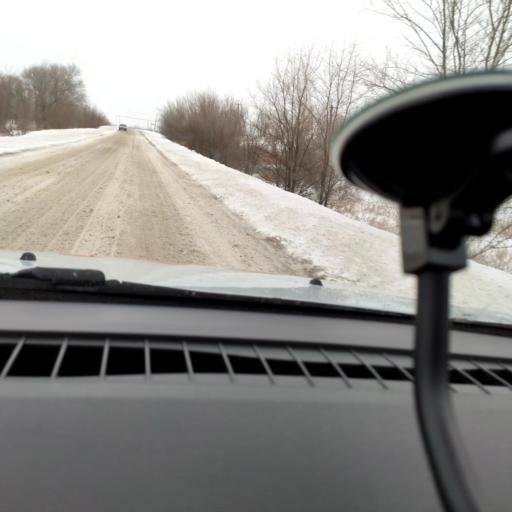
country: RU
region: Samara
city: Dubovyy Umet
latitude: 53.0412
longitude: 50.2381
